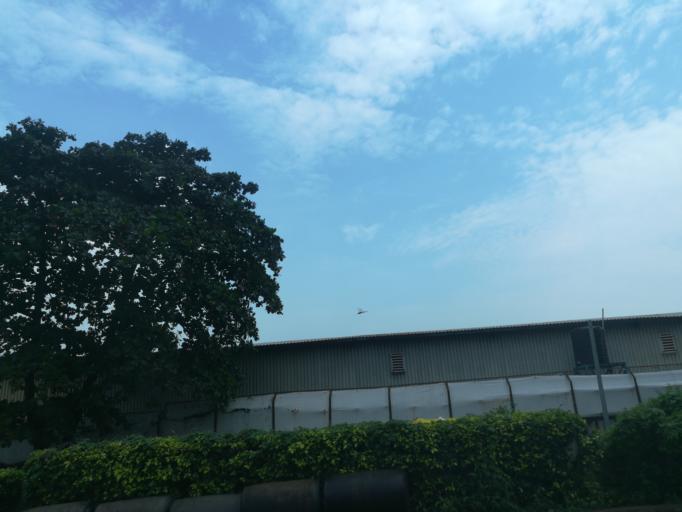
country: NG
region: Lagos
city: Ojota
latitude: 6.6069
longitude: 3.3686
